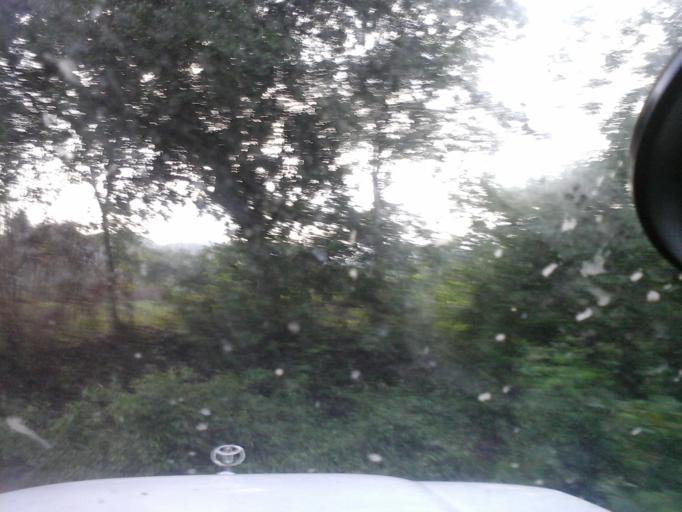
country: CO
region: Cesar
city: Agustin Codazzi
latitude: 10.1734
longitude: -73.1484
